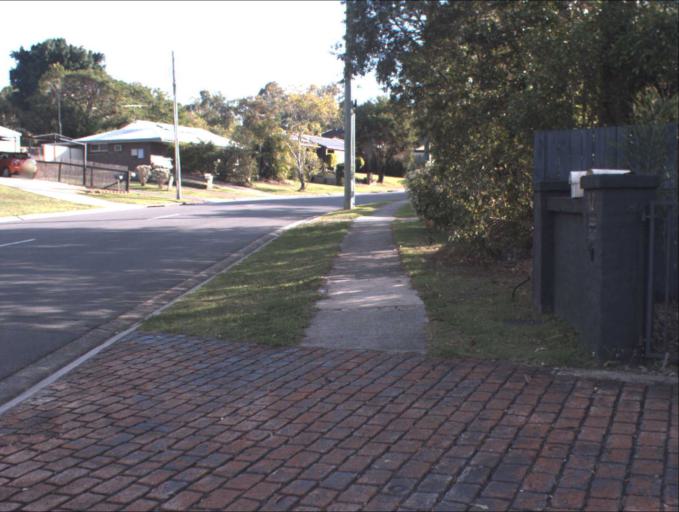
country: AU
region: Queensland
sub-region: Logan
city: Beenleigh
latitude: -27.7068
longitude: 153.1710
